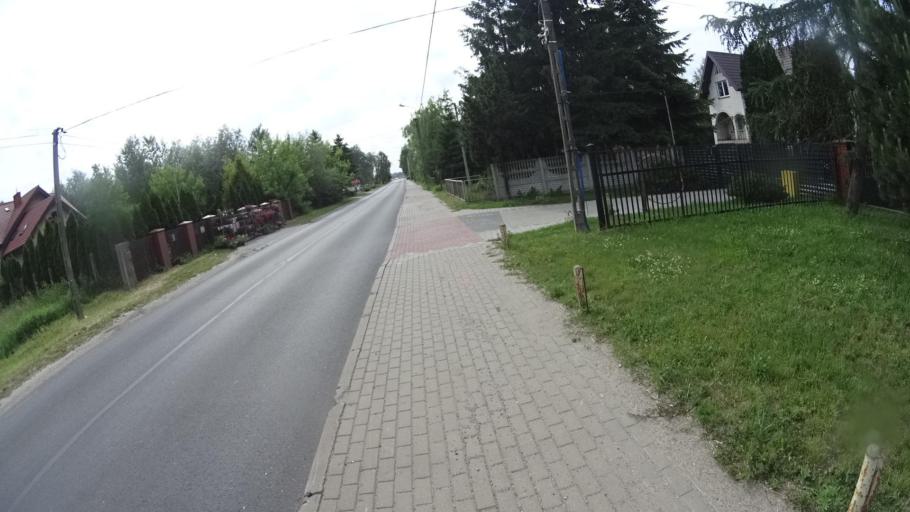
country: PL
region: Masovian Voivodeship
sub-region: Powiat warszawski zachodni
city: Jozefow
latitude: 52.1913
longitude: 20.7467
